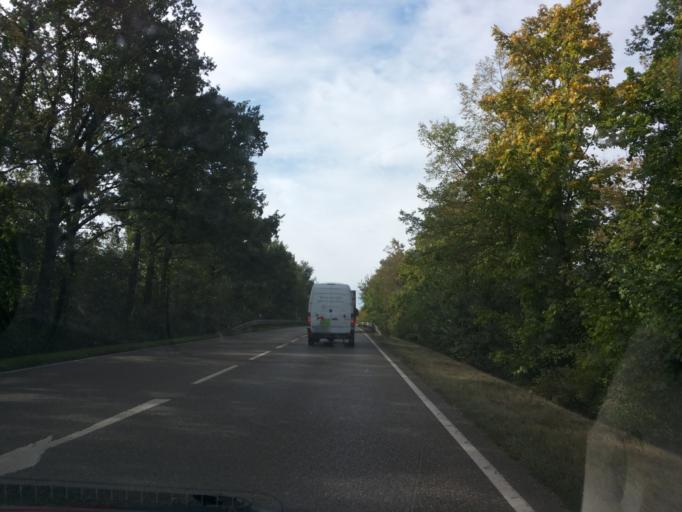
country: DE
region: Bavaria
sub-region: Upper Bavaria
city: Lenting
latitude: 48.7809
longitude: 11.4801
